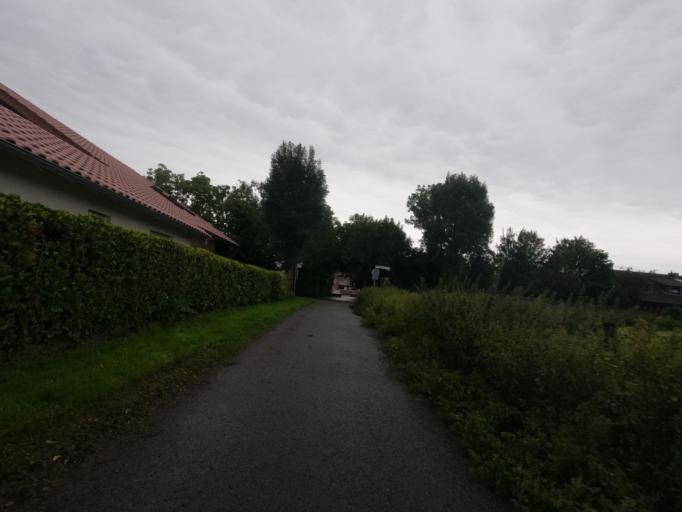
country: DE
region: North Rhine-Westphalia
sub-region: Regierungsbezirk Koln
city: Ubach-Palenberg
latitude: 50.9445
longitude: 6.1588
